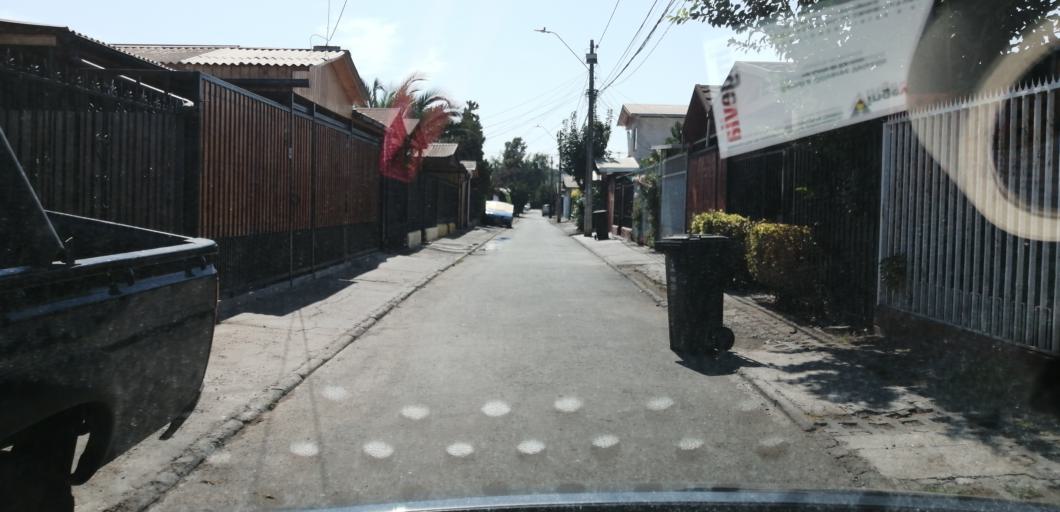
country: CL
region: Santiago Metropolitan
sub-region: Provincia de Santiago
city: Lo Prado
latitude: -33.4657
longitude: -70.7394
